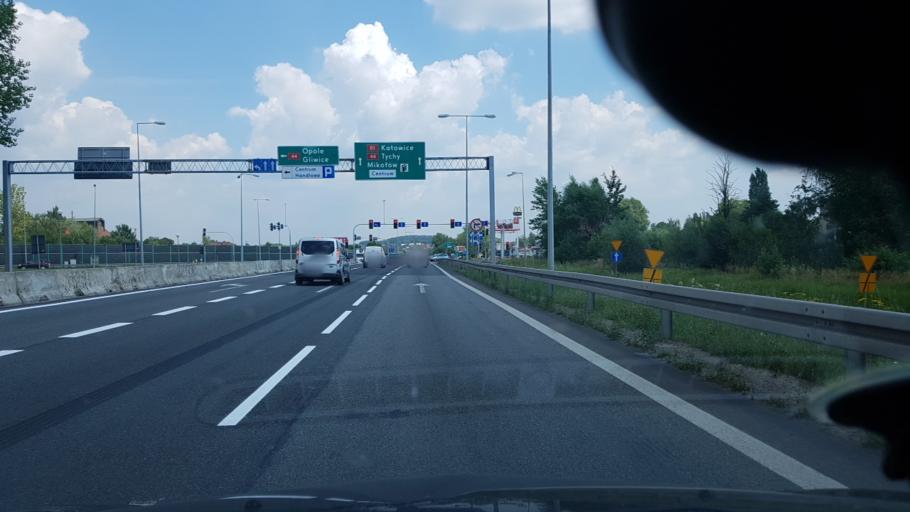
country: PL
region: Silesian Voivodeship
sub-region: Powiat mikolowski
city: Mikolow
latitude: 50.1775
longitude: 18.8891
